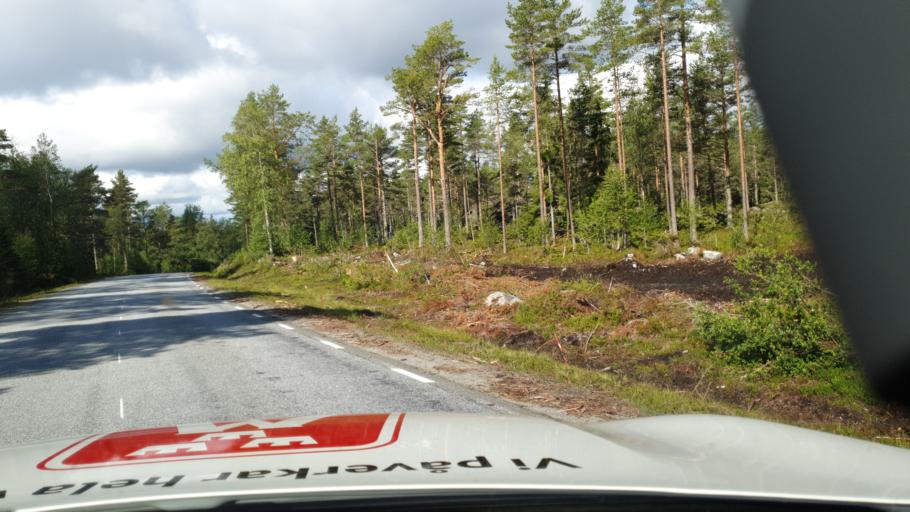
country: SE
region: Vaesterbotten
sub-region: Umea Kommun
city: Roback
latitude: 63.6742
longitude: 20.1258
